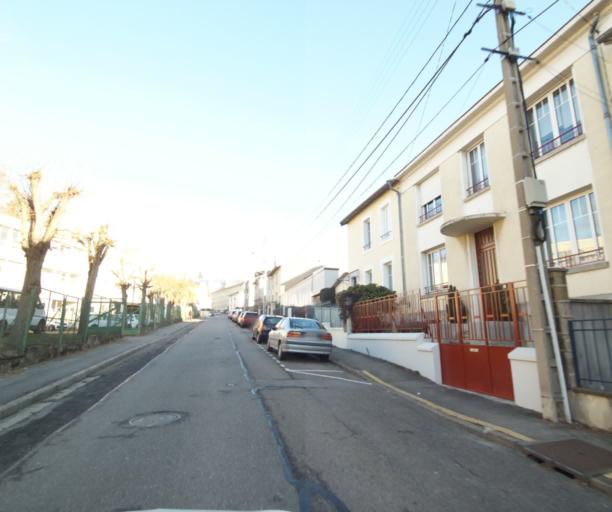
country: FR
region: Lorraine
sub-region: Departement de Meurthe-et-Moselle
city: Laxou
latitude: 48.6878
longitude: 6.1554
